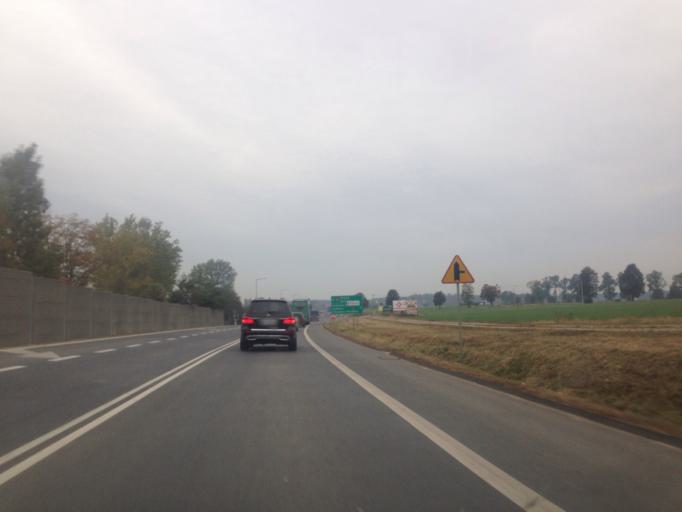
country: PL
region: Greater Poland Voivodeship
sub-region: Powiat gnieznienski
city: Niechanowo
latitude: 52.5531
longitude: 17.7048
